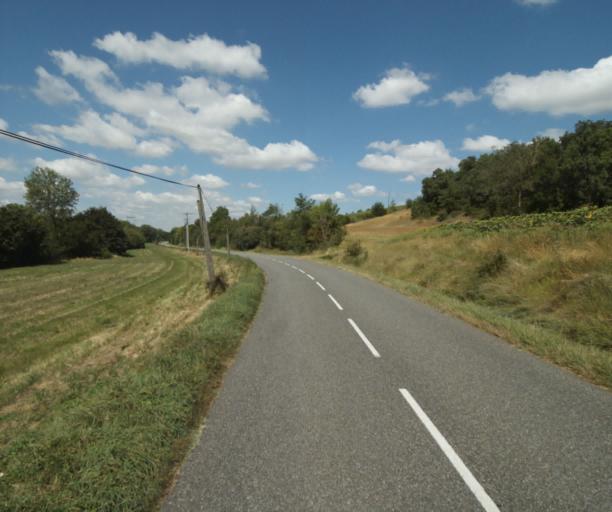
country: FR
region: Midi-Pyrenees
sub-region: Departement de la Haute-Garonne
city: Auriac-sur-Vendinelle
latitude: 43.4799
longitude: 1.8003
